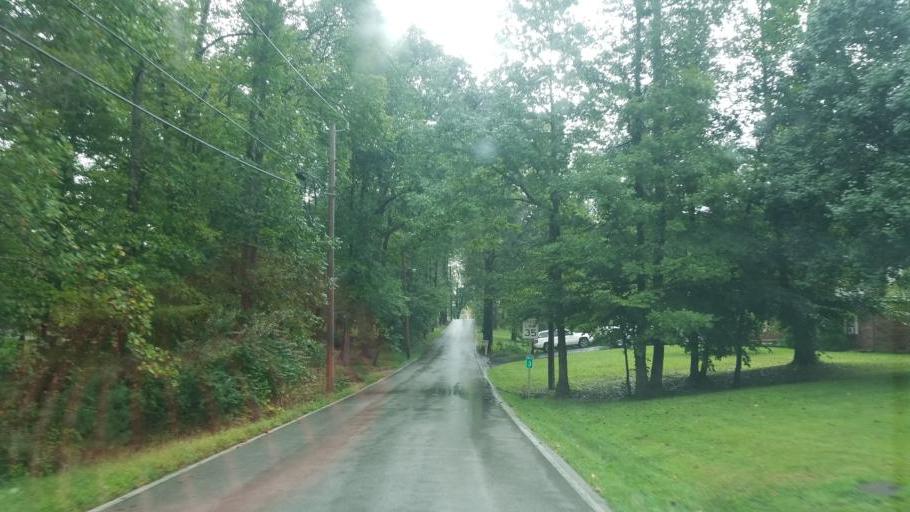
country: US
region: Kentucky
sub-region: Rowan County
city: Morehead
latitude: 38.1802
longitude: -83.4858
